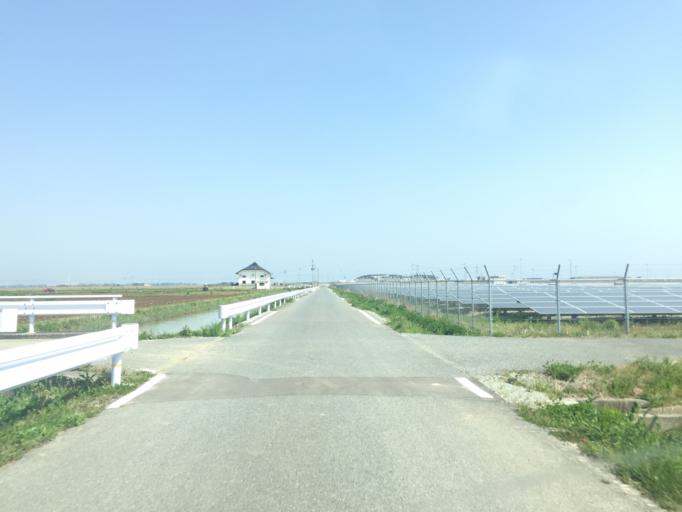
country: JP
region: Miyagi
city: Marumori
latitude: 37.7714
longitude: 140.9775
